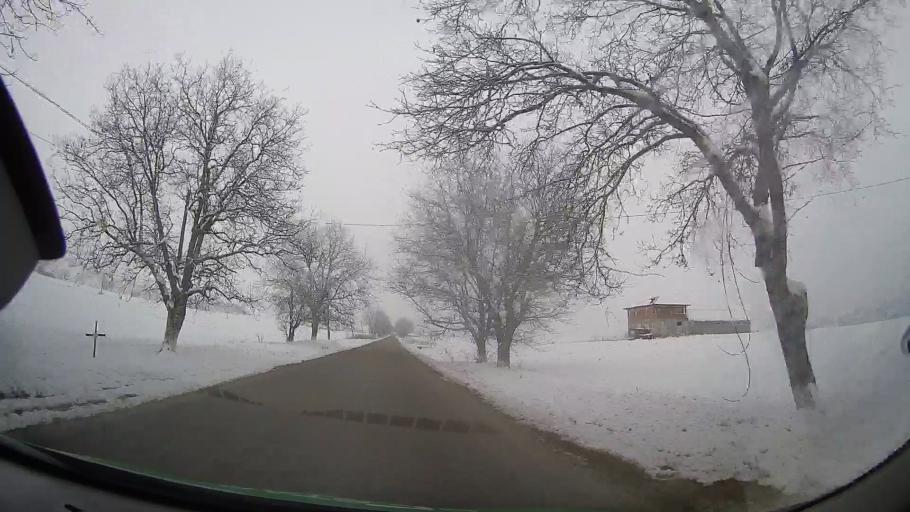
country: RO
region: Bacau
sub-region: Comuna Oncesti
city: Oncesti
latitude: 46.4499
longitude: 27.2625
